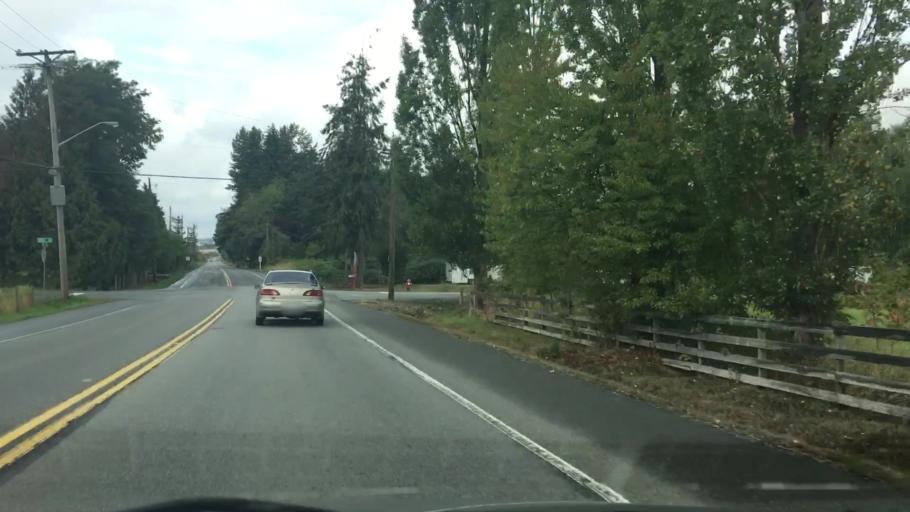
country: CA
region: British Columbia
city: Langley
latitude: 49.1045
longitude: -122.6036
